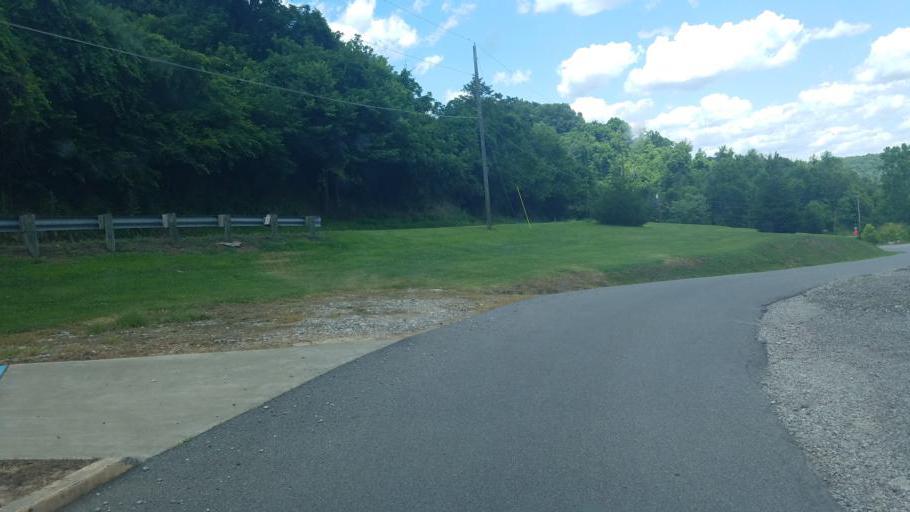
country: US
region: Ohio
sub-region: Gallia County
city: Gallipolis
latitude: 38.8004
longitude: -82.2256
